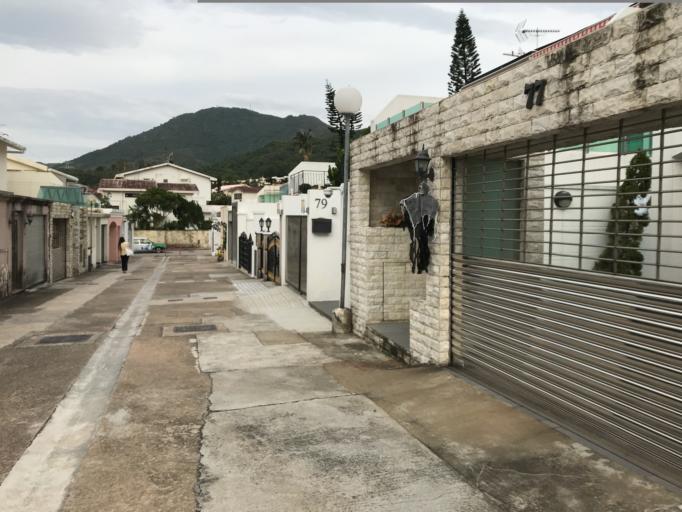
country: HK
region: Tai Po
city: Tai Po
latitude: 22.4629
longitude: 114.1547
